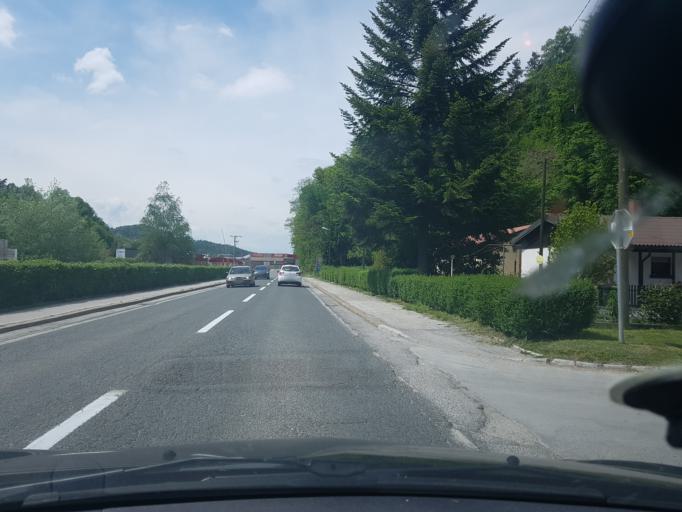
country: SI
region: Store
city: Store
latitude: 46.2223
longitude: 15.3197
